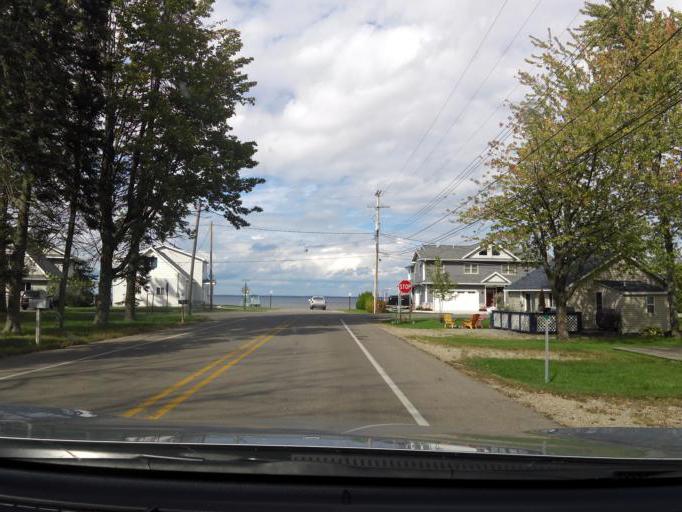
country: US
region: Michigan
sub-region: Roscommon County
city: Houghton Lake
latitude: 44.2993
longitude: -84.7123
